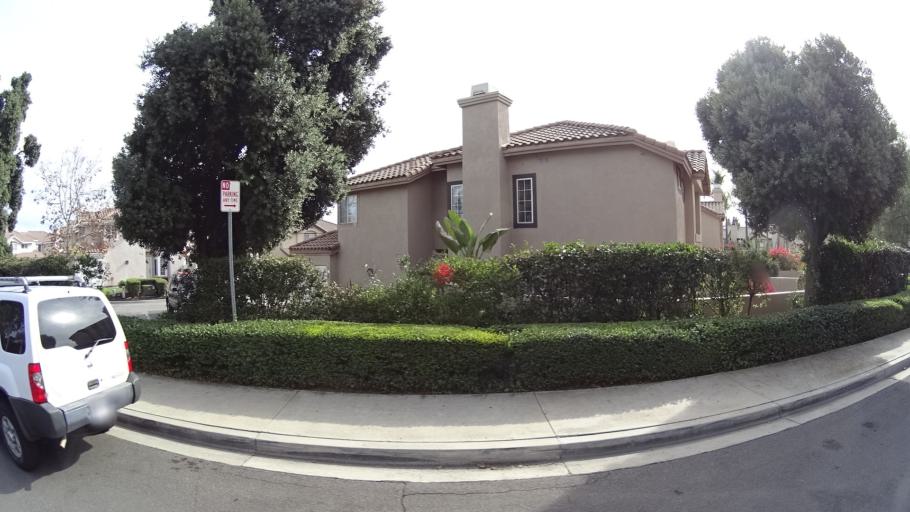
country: US
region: California
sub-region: Orange County
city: Aliso Viejo
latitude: 33.5742
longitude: -117.7202
